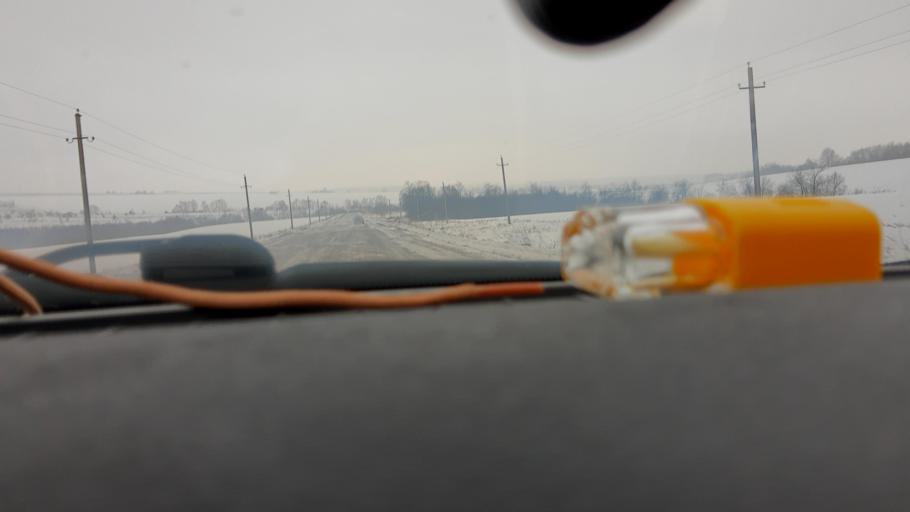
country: RU
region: Bashkortostan
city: Ulukulevo
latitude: 54.5322
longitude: 56.4304
